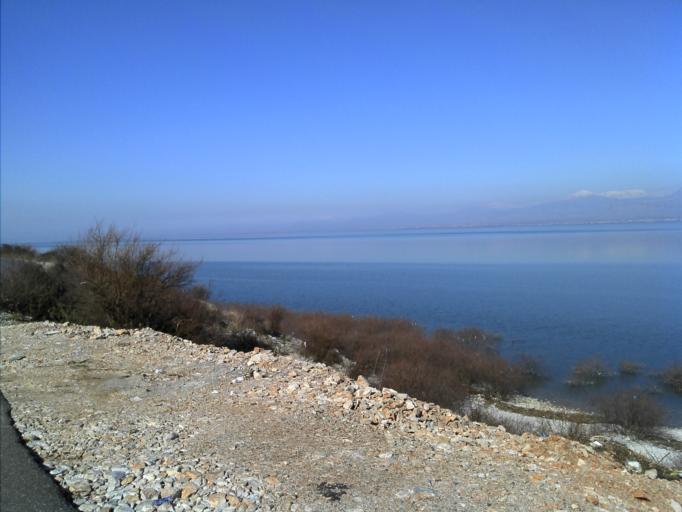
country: AL
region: Shkoder
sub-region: Rrethi i Shkodres
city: Berdica e Madhe
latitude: 42.0632
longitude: 19.4389
